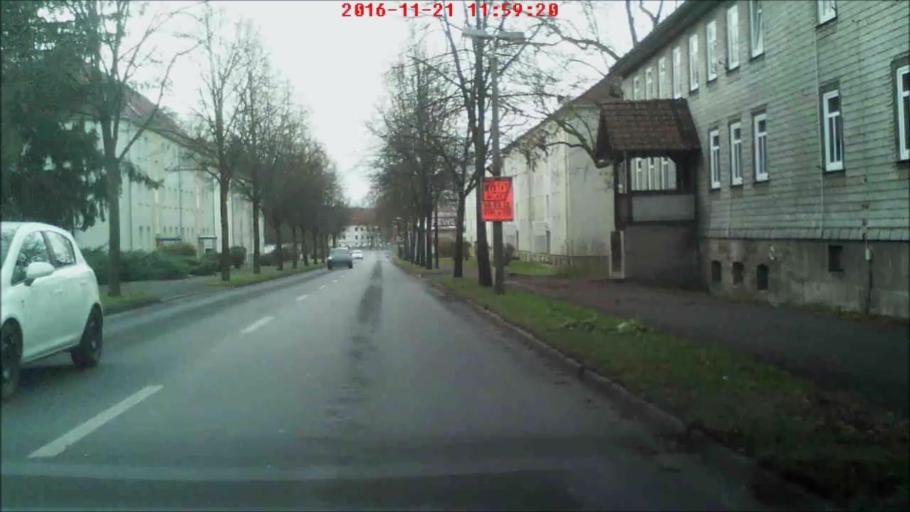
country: DE
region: Thuringia
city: Schleusingen
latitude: 50.5078
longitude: 10.7465
